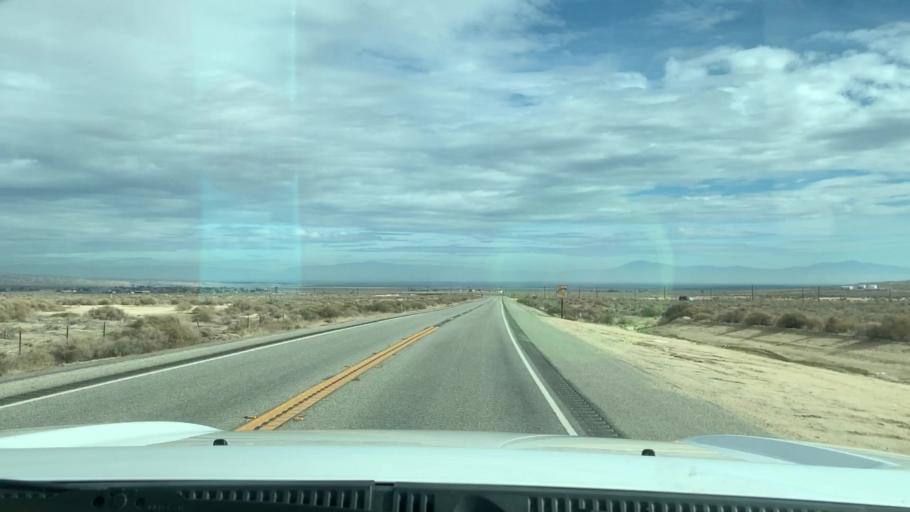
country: US
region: California
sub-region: Kern County
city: Ford City
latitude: 35.1871
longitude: -119.4438
